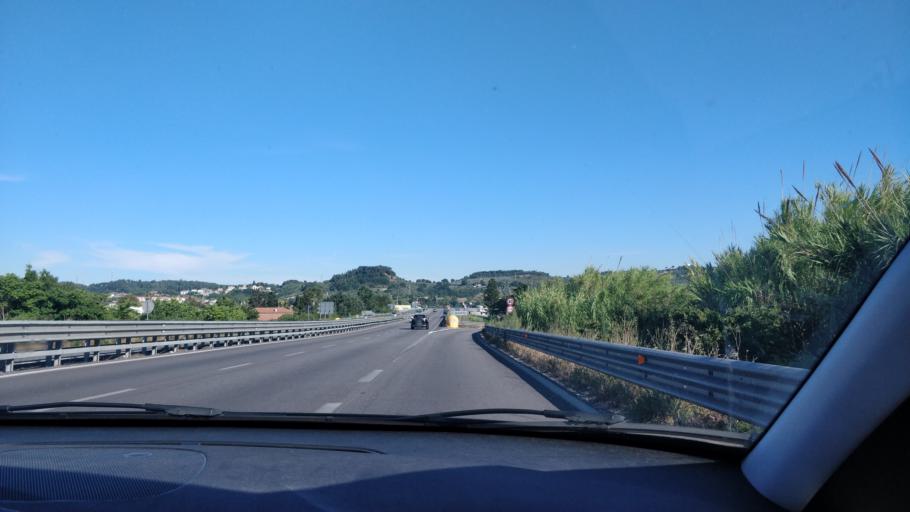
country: IT
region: Abruzzo
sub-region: Provincia di Pescara
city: Villa Raspa
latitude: 42.4439
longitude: 14.1925
